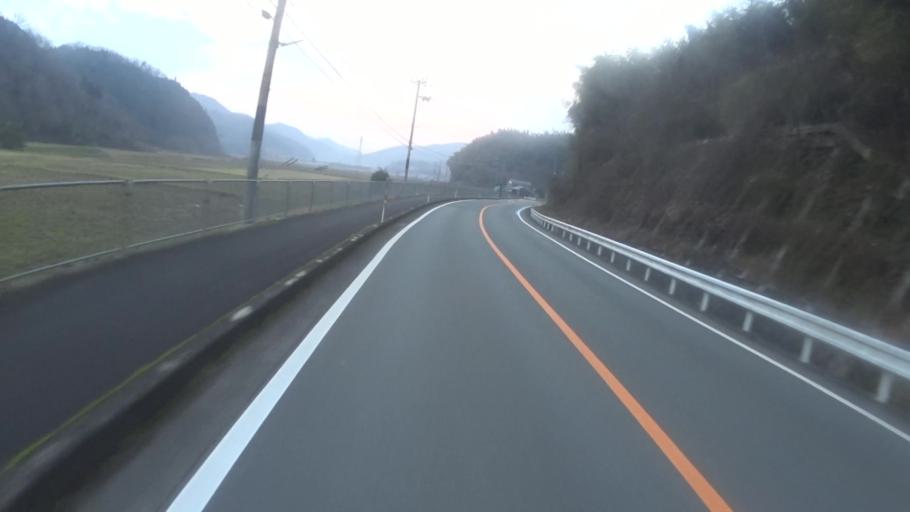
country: JP
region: Kyoto
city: Maizuru
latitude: 35.3397
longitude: 135.3577
